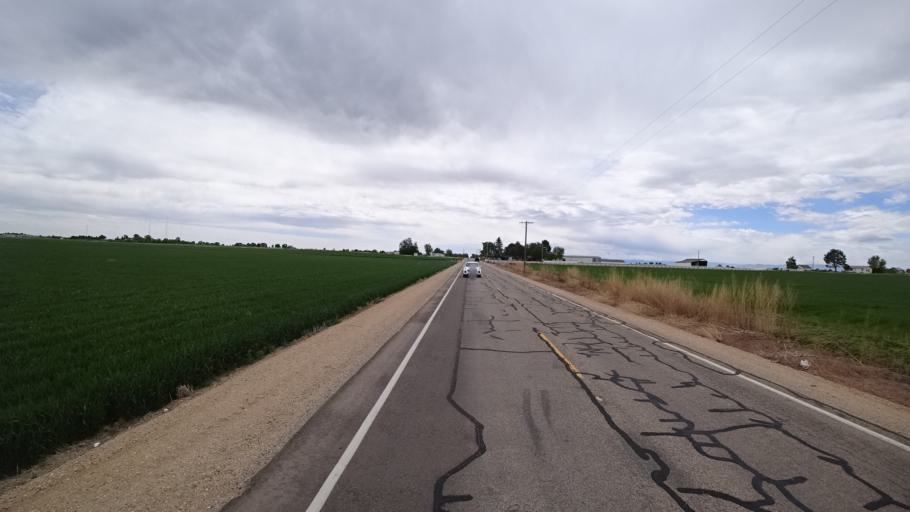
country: US
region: Idaho
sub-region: Ada County
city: Meridian
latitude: 43.5699
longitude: -116.4138
